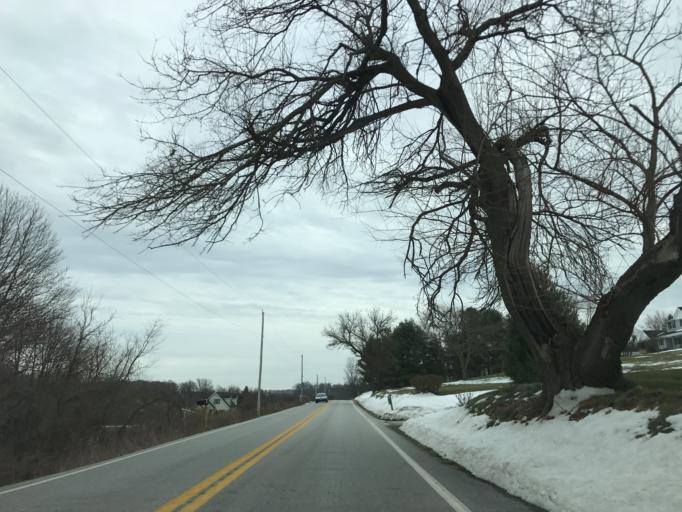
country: US
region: Pennsylvania
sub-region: York County
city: New Freedom
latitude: 39.7271
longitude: -76.7270
